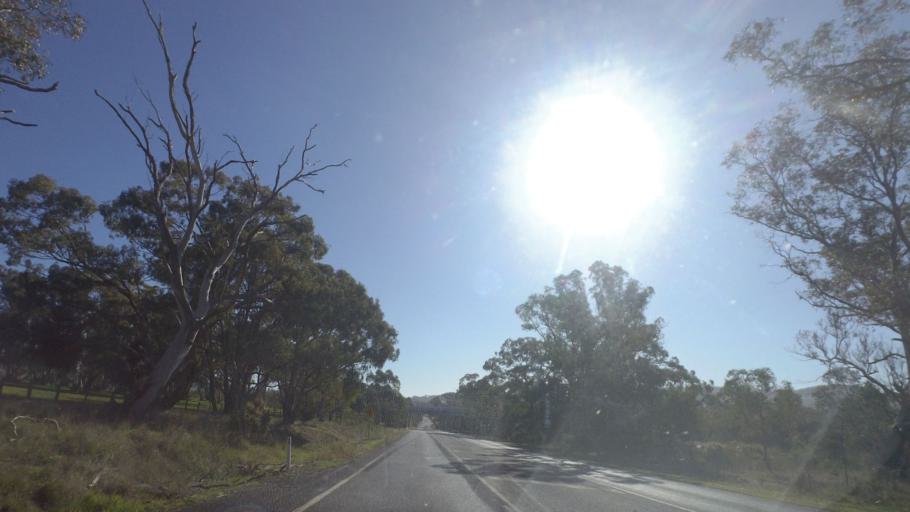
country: AU
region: Victoria
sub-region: Mount Alexander
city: Castlemaine
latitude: -37.0508
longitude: 144.2924
